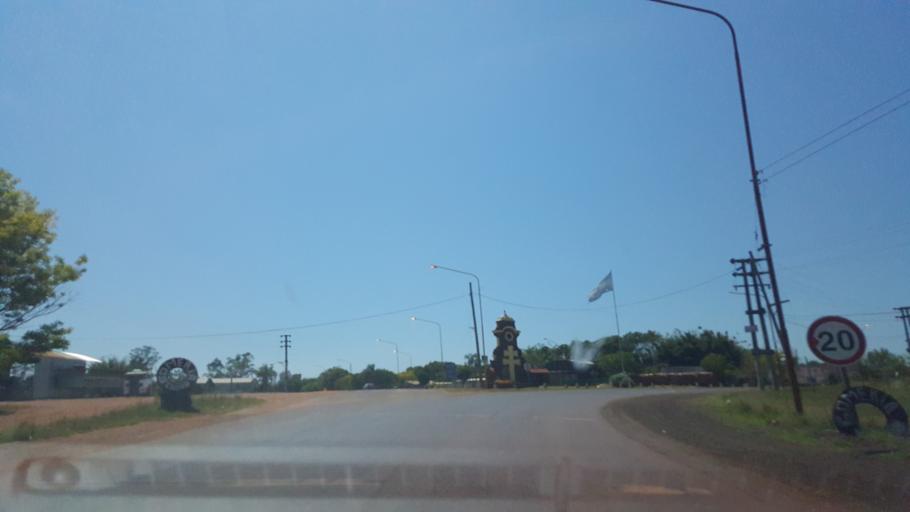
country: AR
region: Corrientes
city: Santo Tome
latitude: -28.5506
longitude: -56.0727
